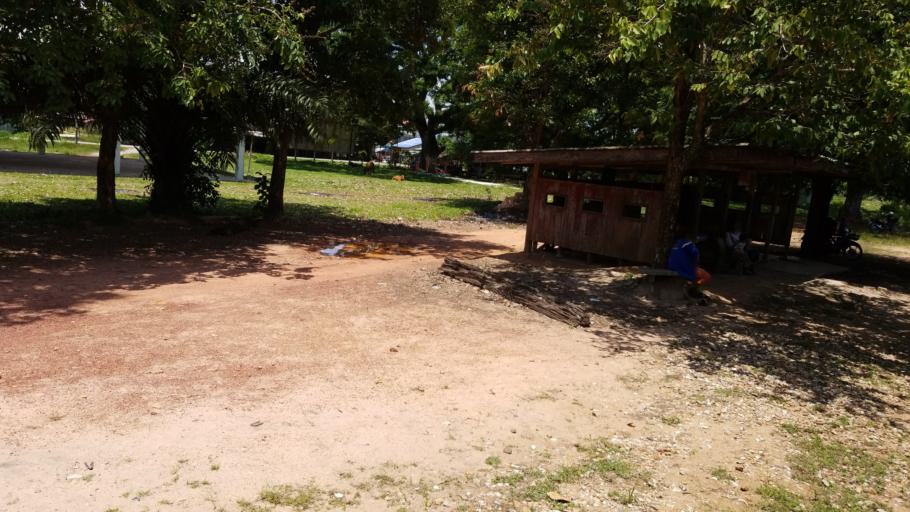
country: TH
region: Phatthalung
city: Bang Kaeo
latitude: 7.3759
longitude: 100.2012
